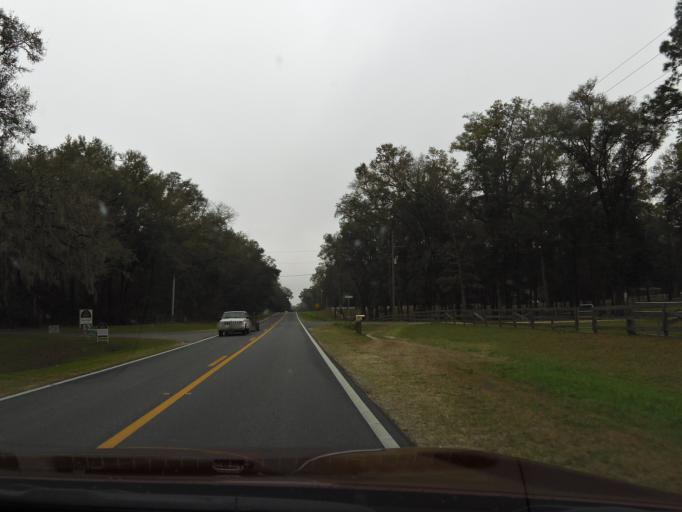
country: US
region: Florida
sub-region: Alachua County
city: High Springs
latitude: 29.8541
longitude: -82.5748
